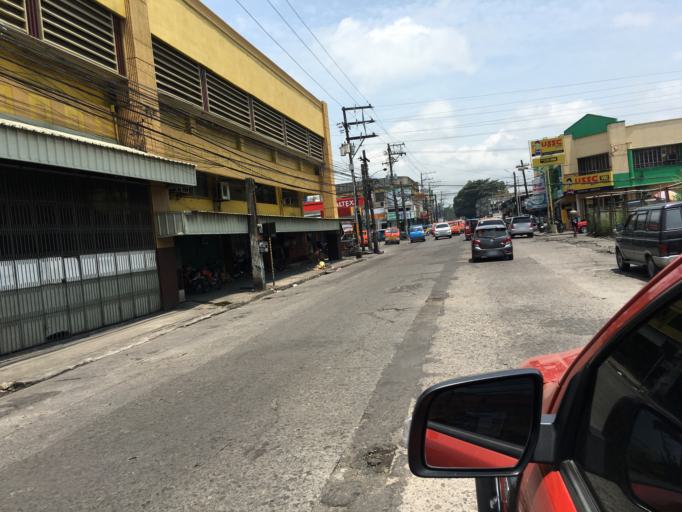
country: PH
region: Western Visayas
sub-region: Province of Negros Occidental
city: Bacolod City
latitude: 10.6612
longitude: 122.9487
